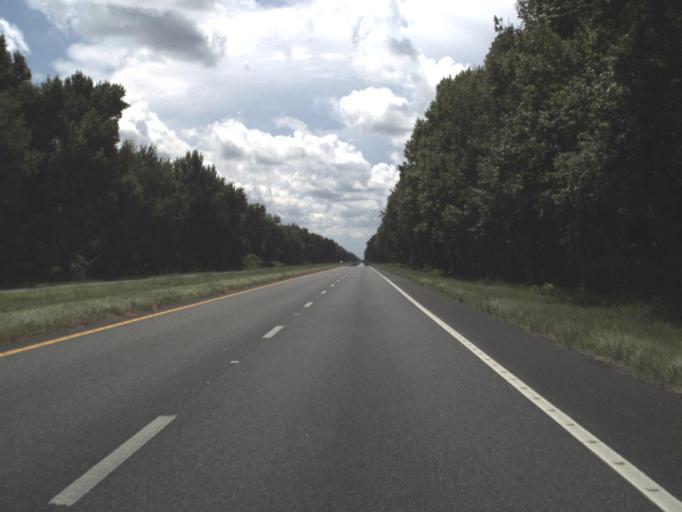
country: US
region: Florida
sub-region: Taylor County
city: Perry
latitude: 30.2442
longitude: -83.6948
